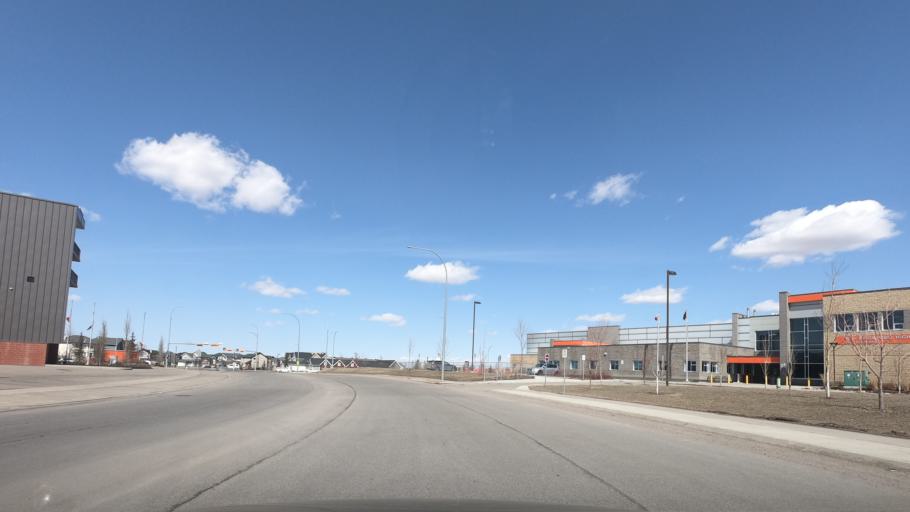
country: CA
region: Alberta
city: Airdrie
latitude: 51.2695
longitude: -114.0285
